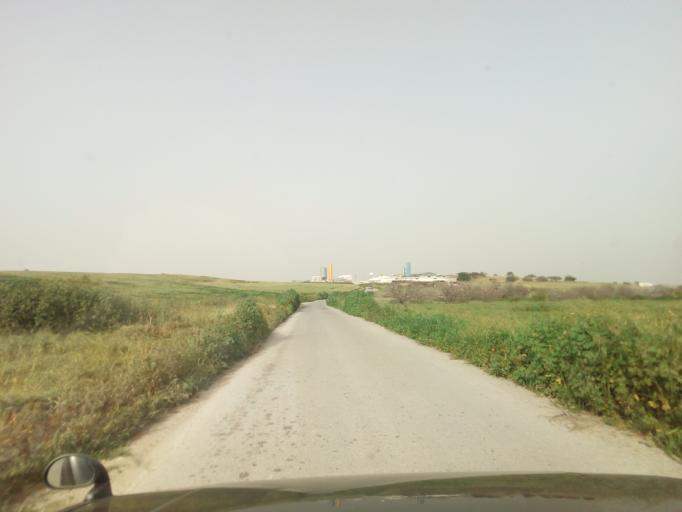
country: CY
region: Larnaka
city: Athienou
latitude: 35.0414
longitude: 33.5325
